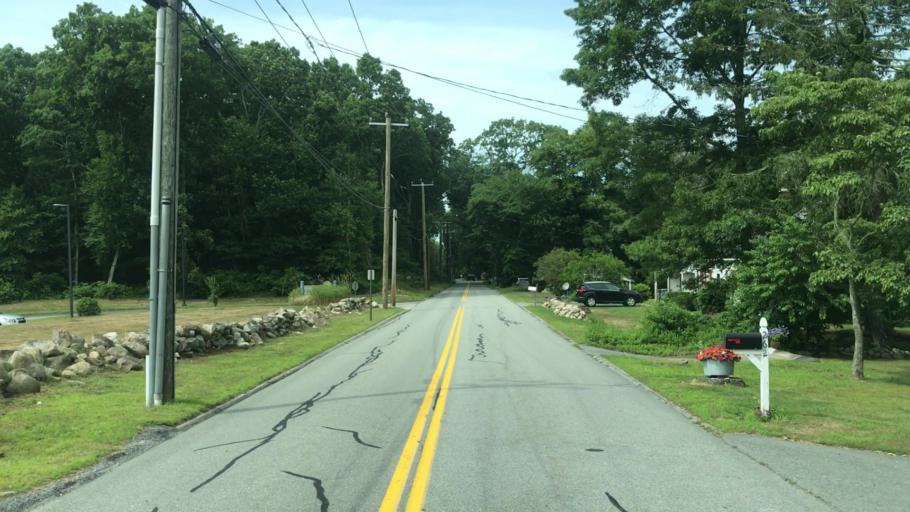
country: US
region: Connecticut
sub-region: New London County
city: Niantic
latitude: 41.3207
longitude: -72.2303
